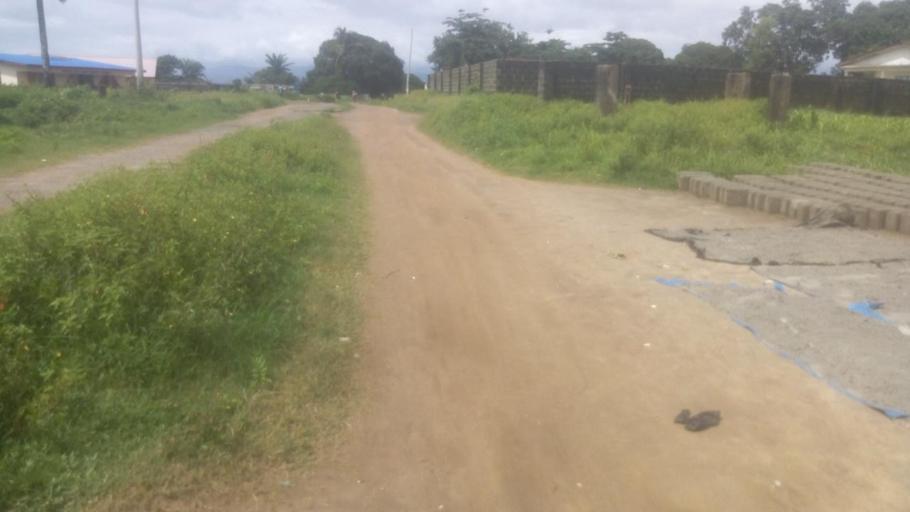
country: SL
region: Northern Province
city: Masoyila
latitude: 8.5878
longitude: -13.1996
